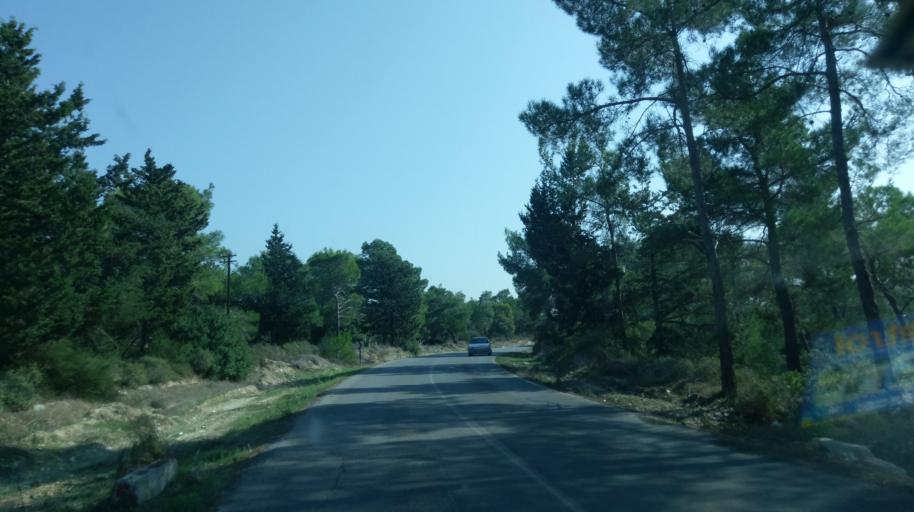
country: CY
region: Keryneia
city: Lapithos
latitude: 35.3284
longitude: 33.0396
